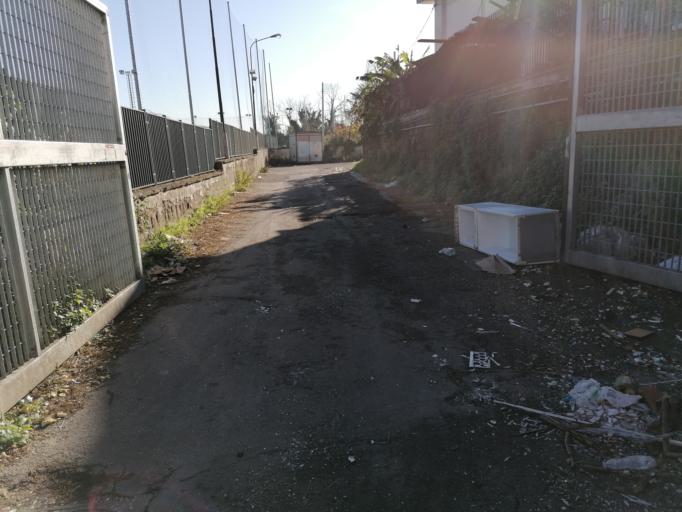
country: IT
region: Campania
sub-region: Provincia di Napoli
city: Casavatore
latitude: 40.8853
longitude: 14.2622
